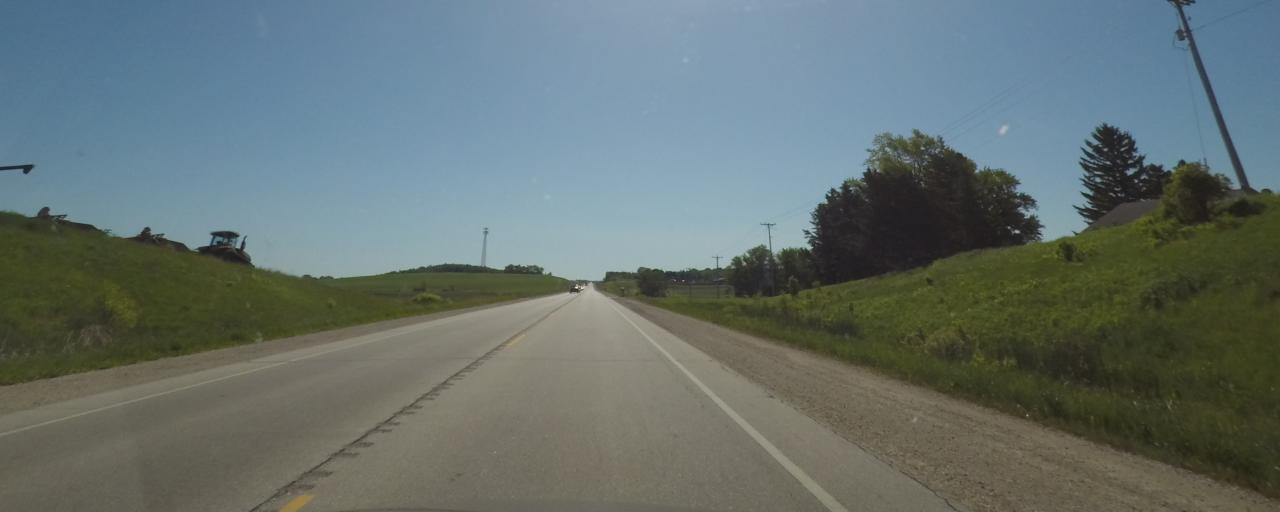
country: US
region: Wisconsin
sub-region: Fond du Lac County
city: Saint Peter
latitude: 43.7832
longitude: -88.3127
